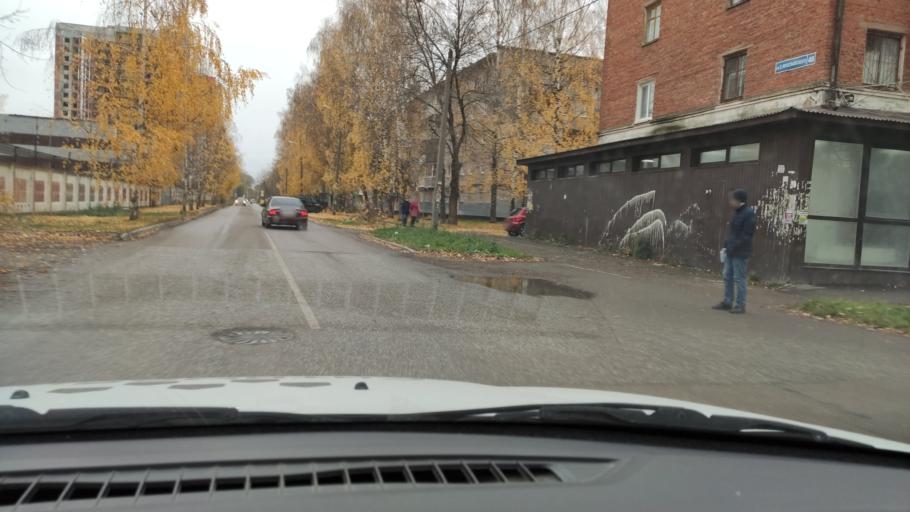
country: RU
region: Perm
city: Perm
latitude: 57.9685
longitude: 56.2288
